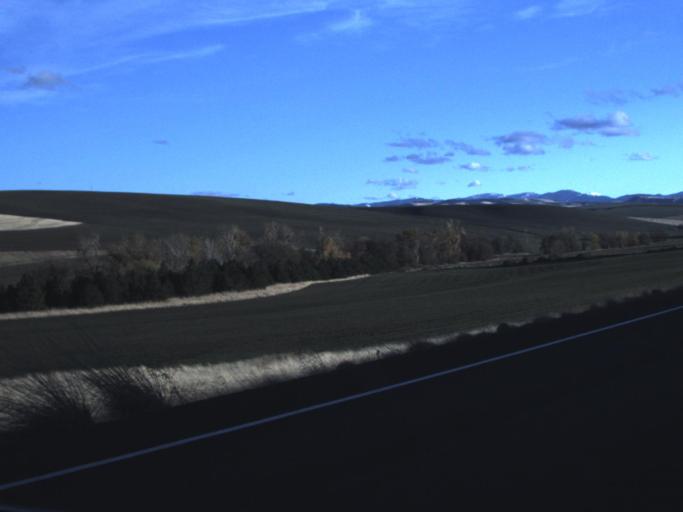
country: US
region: Washington
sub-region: Walla Walla County
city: Waitsburg
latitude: 46.2473
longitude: -118.1461
